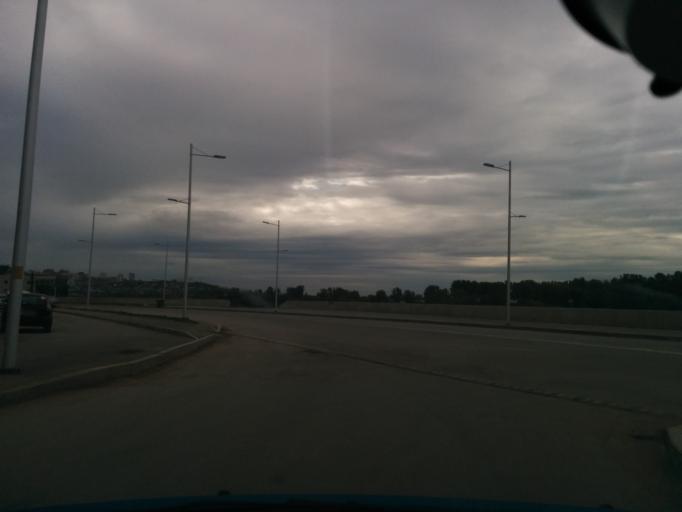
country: RU
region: Bashkortostan
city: Ufa
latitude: 54.7152
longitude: 55.9312
